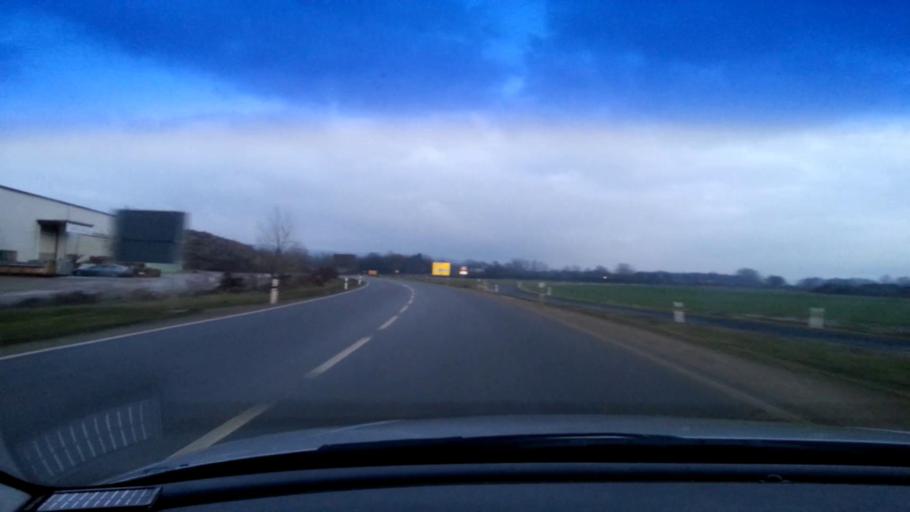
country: DE
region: Bavaria
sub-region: Upper Franconia
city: Pettstadt
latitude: 49.8296
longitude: 10.9443
